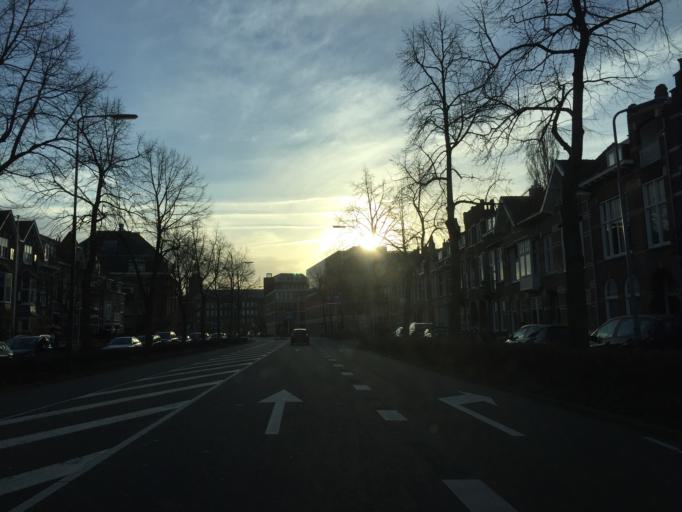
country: NL
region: North Brabant
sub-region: Gemeente 's-Hertogenbosch
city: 's-Hertogenbosch
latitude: 51.6866
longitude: 5.2941
